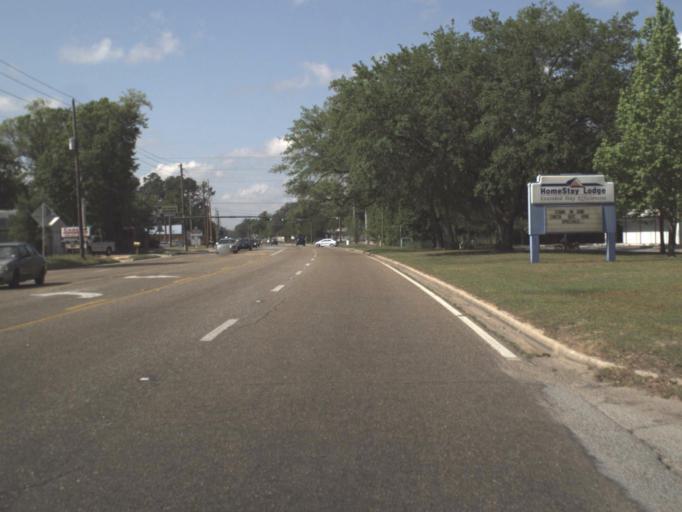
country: US
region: Florida
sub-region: Escambia County
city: Ferry Pass
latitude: 30.5316
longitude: -87.2072
